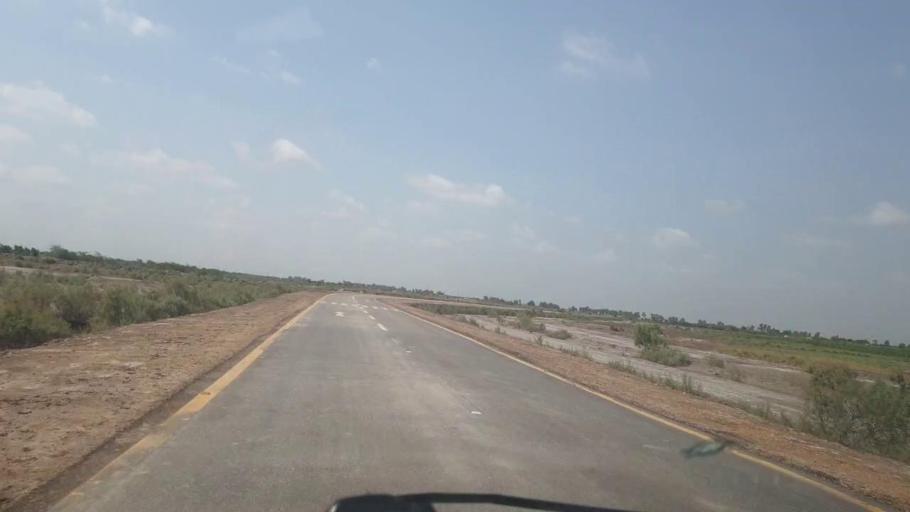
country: PK
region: Sindh
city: Berani
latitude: 25.7159
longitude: 68.9451
